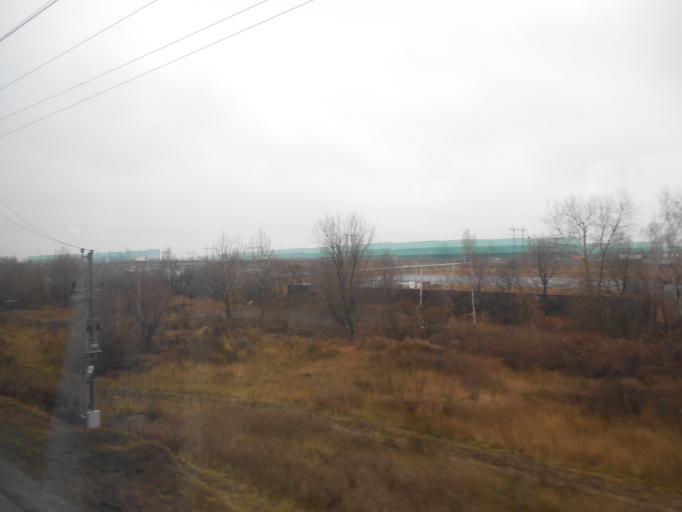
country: RU
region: Moskovskaya
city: Yam
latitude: 55.4817
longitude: 37.7395
